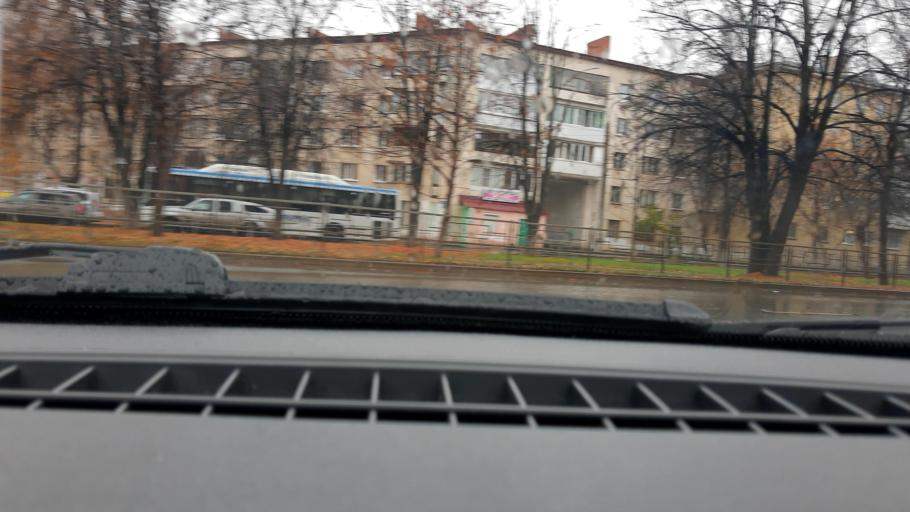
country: RU
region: Bashkortostan
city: Ufa
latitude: 54.8153
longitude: 56.1043
